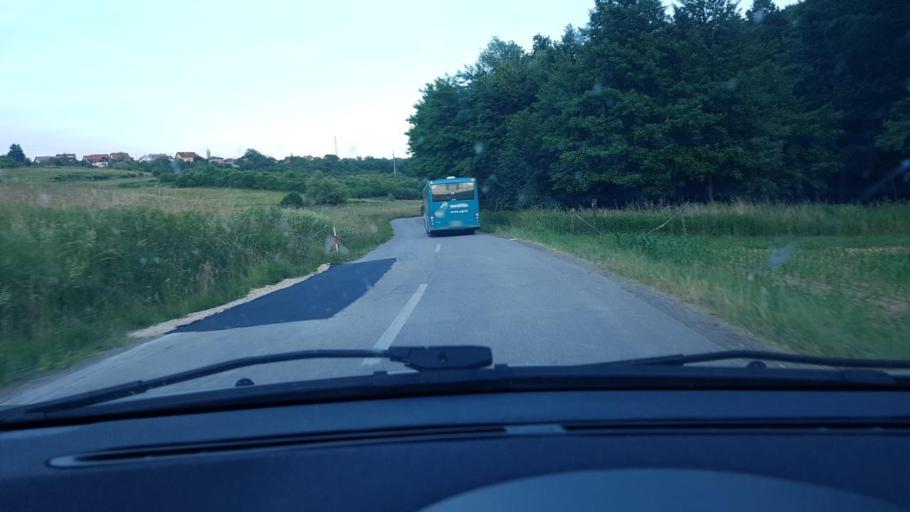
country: HR
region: Varazdinska
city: Remetinec
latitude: 46.1973
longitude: 16.3213
